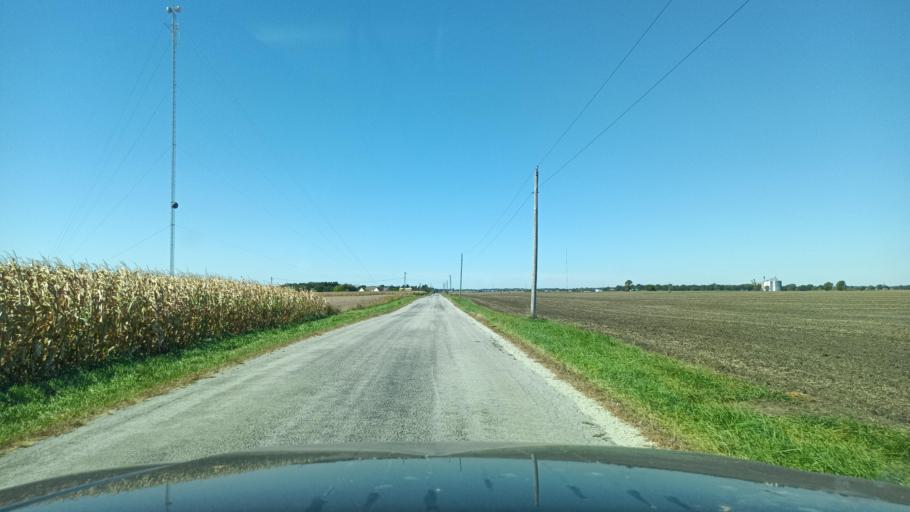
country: US
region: Illinois
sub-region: Champaign County
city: Mahomet
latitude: 40.0987
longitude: -88.3995
